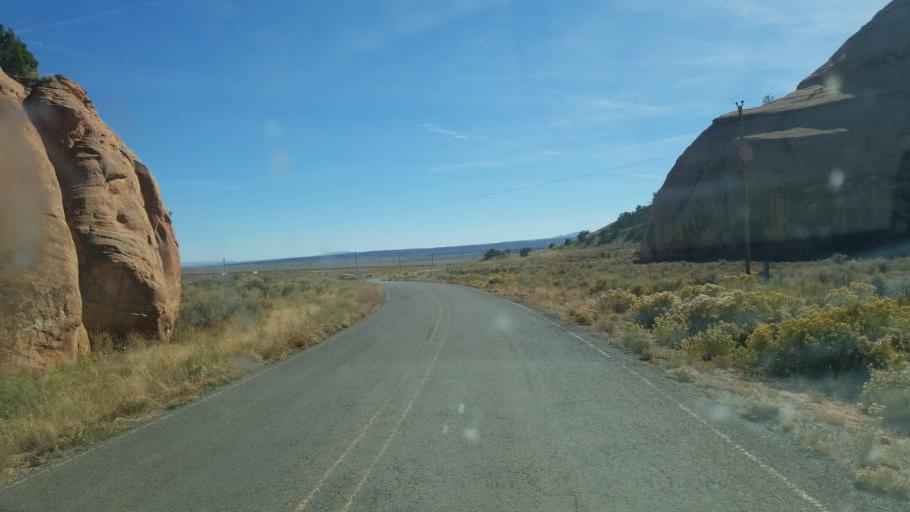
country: US
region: New Mexico
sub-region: McKinley County
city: Thoreau
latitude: 35.4338
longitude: -108.0512
